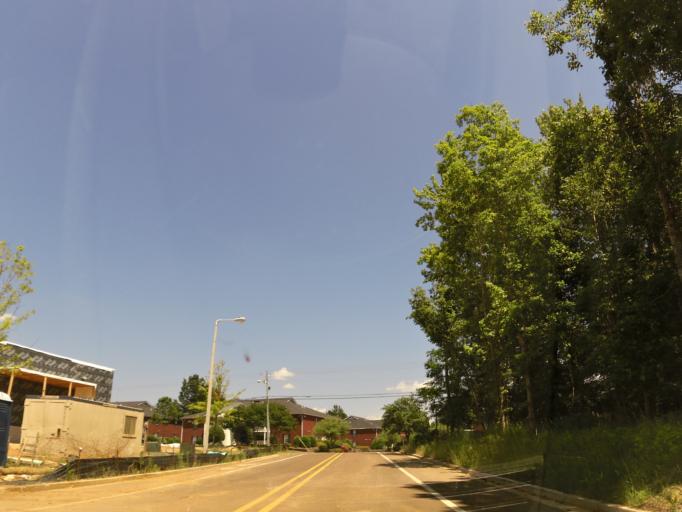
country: US
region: Mississippi
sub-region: Lafayette County
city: University
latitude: 34.3407
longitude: -89.5478
